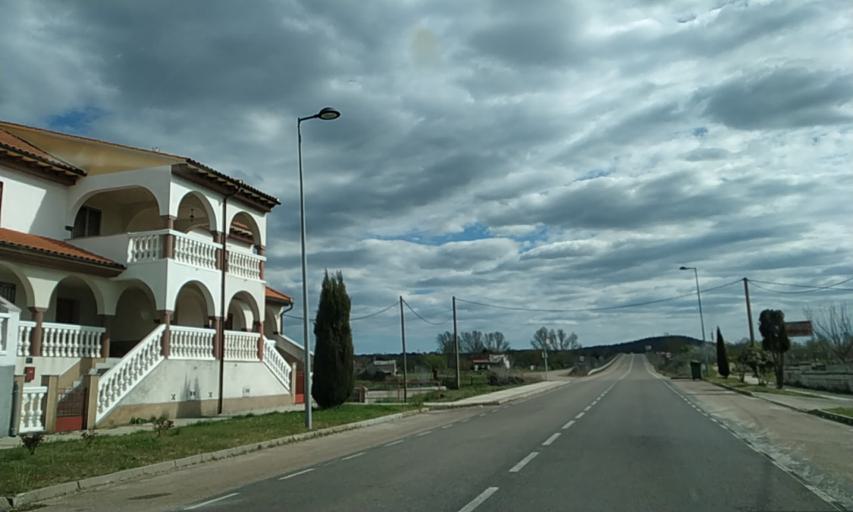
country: ES
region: Castille and Leon
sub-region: Provincia de Salamanca
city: Ciudad Rodrigo
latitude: 40.5884
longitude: -6.5373
